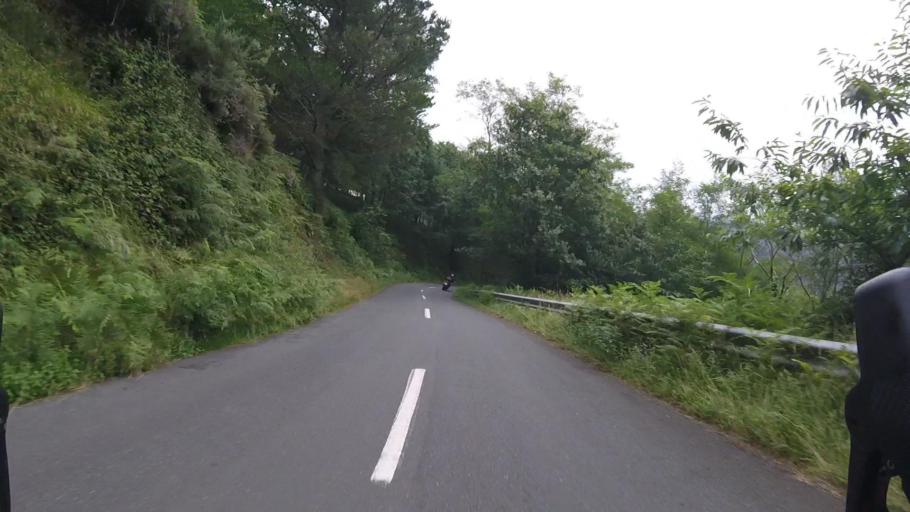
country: ES
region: Basque Country
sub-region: Provincia de Guipuzcoa
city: Irun
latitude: 43.2730
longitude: -1.8085
